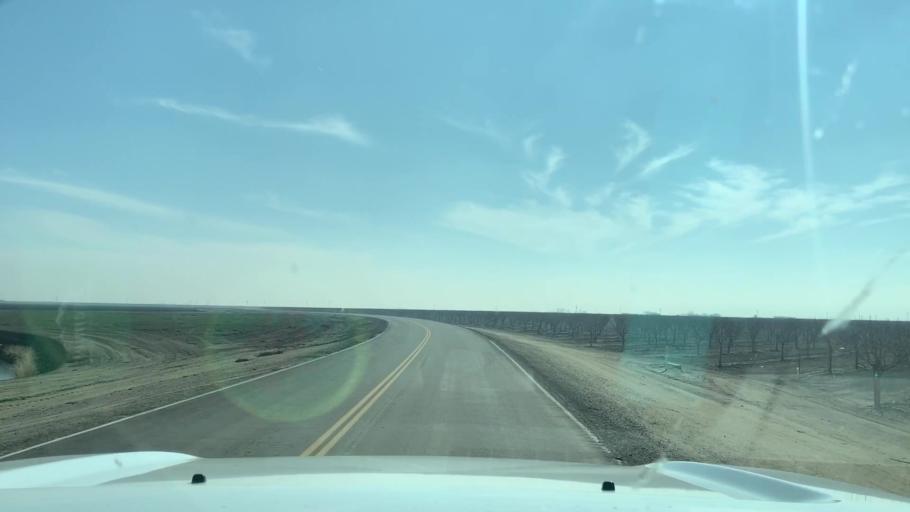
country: US
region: California
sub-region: Kern County
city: Buttonwillow
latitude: 35.4485
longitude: -119.5598
